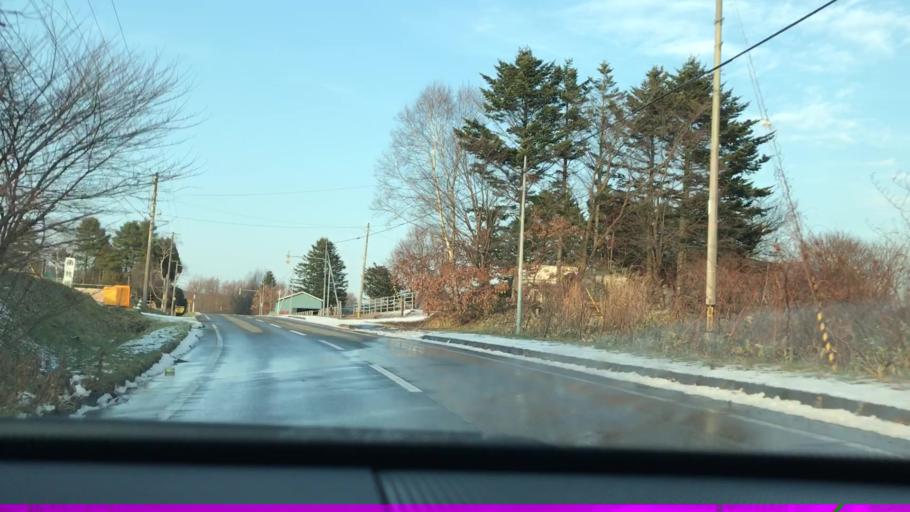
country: JP
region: Hokkaido
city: Shizunai-furukawacho
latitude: 42.4267
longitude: 142.4038
